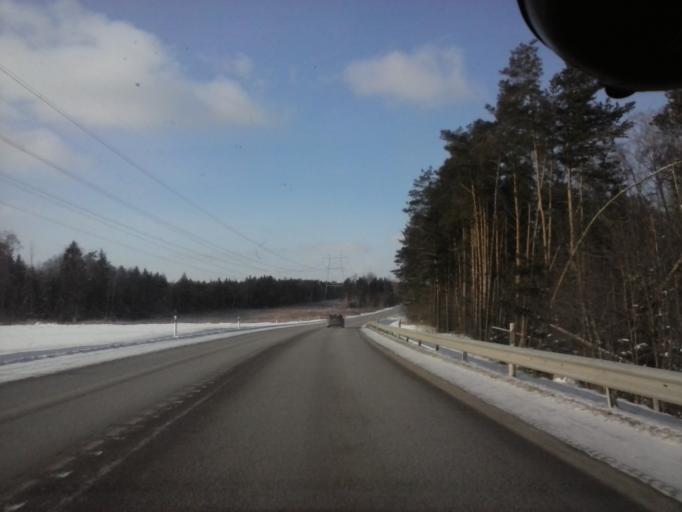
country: EE
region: Tartu
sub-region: Noo vald
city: Noo
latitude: 58.3452
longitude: 26.4878
